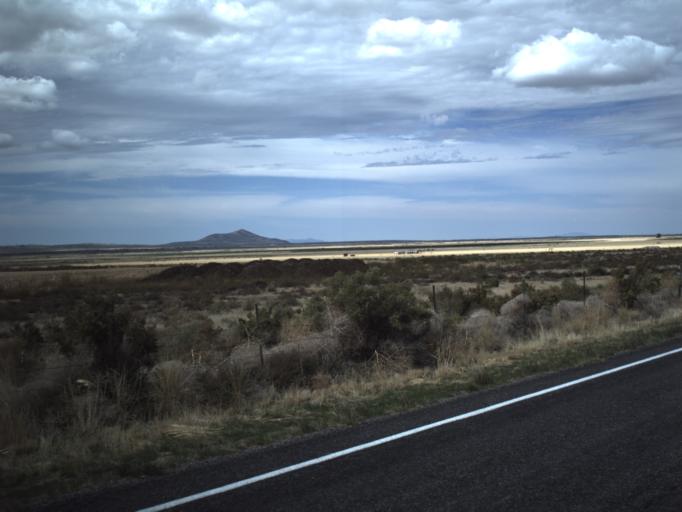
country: US
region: Utah
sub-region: Millard County
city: Fillmore
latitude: 39.0152
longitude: -112.4099
